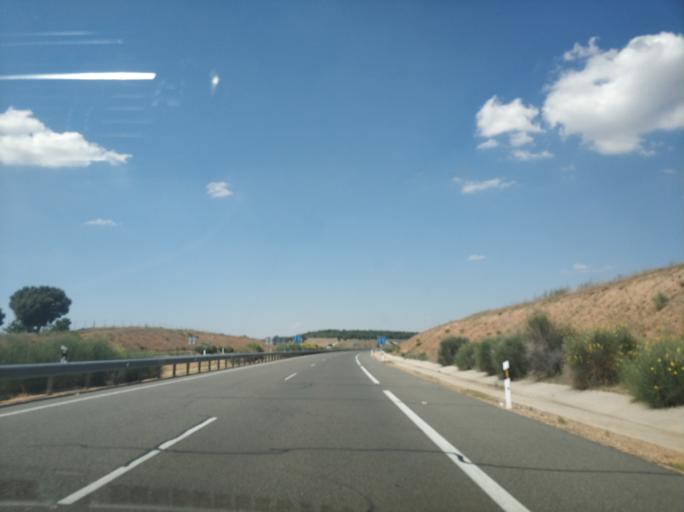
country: ES
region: Castille and Leon
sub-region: Provincia de Zamora
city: Cuelgamures
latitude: 41.2707
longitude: -5.7059
